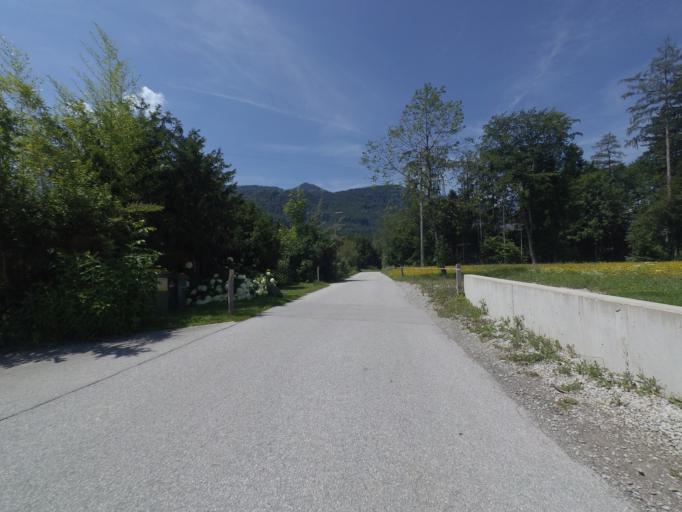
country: AT
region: Salzburg
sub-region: Politischer Bezirk Hallein
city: Adnet
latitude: 47.6537
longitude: 13.1329
